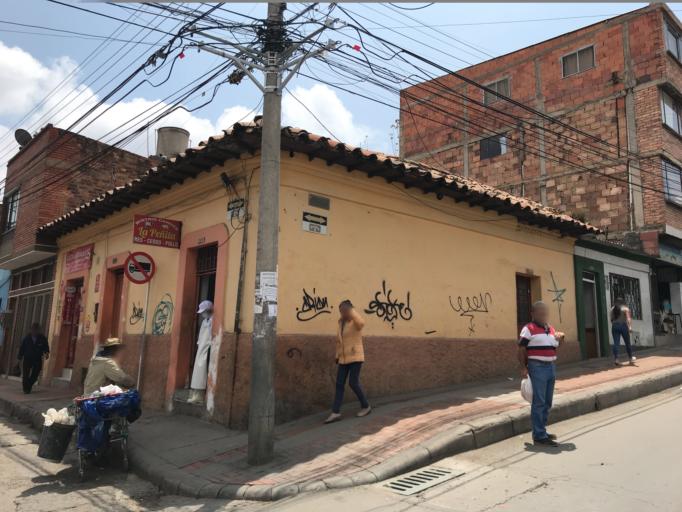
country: CO
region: Boyaca
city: Tunja
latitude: 5.5366
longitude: -73.3658
